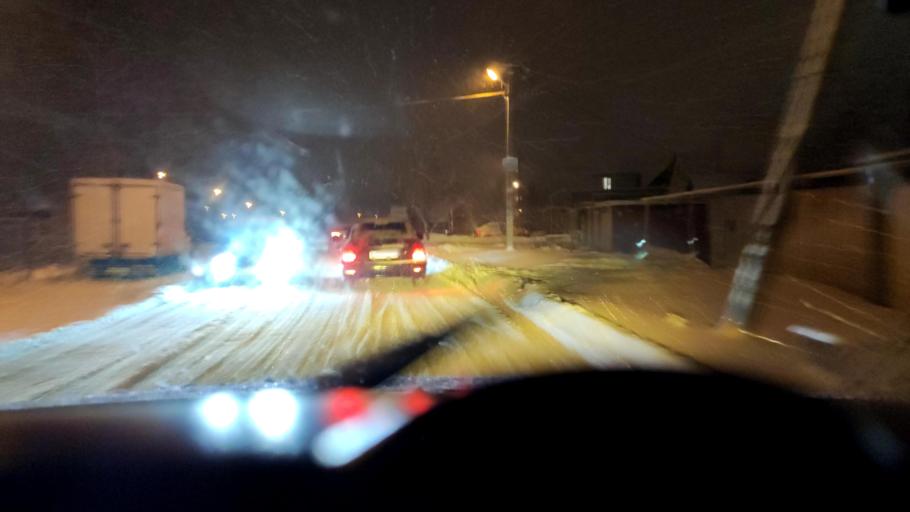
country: RU
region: Voronezj
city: Pridonskoy
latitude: 51.6707
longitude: 39.0797
